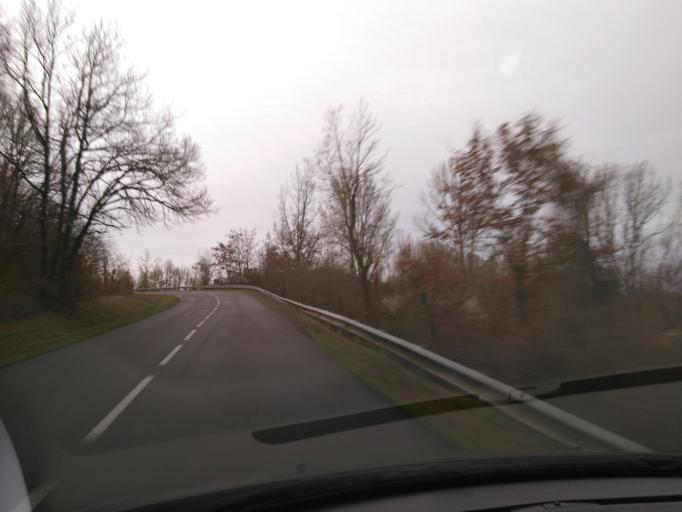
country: FR
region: Midi-Pyrenees
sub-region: Departement du Tarn-et-Garonne
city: Verdun-sur-Garonne
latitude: 43.8405
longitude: 1.1563
